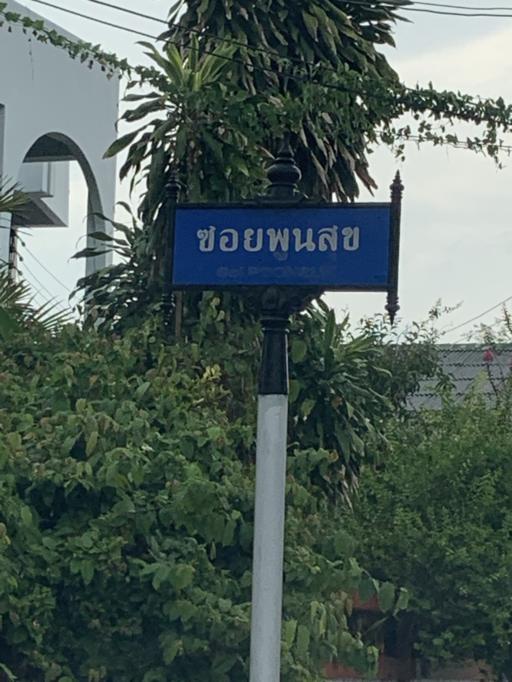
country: TH
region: Yala
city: Yala
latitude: 6.5408
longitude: 101.2869
